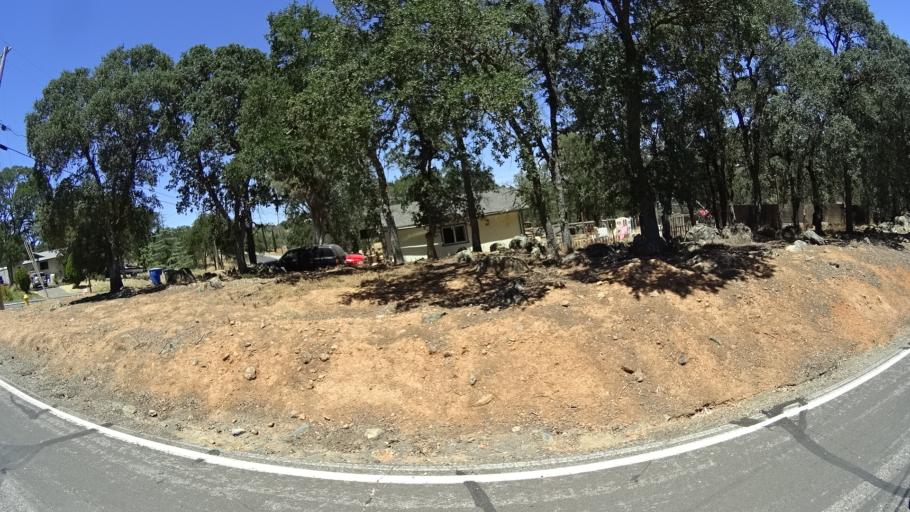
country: US
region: California
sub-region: Calaveras County
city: Rancho Calaveras
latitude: 38.1444
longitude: -120.8378
